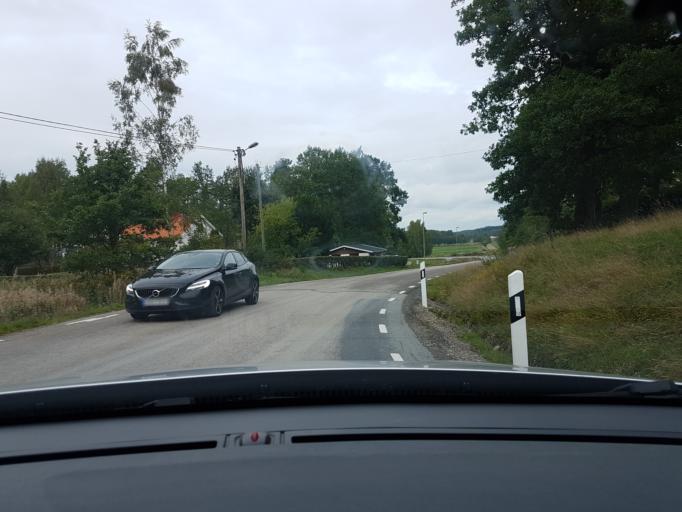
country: SE
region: Vaestra Goetaland
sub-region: Ale Kommun
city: Alvangen
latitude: 57.9136
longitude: 12.1442
